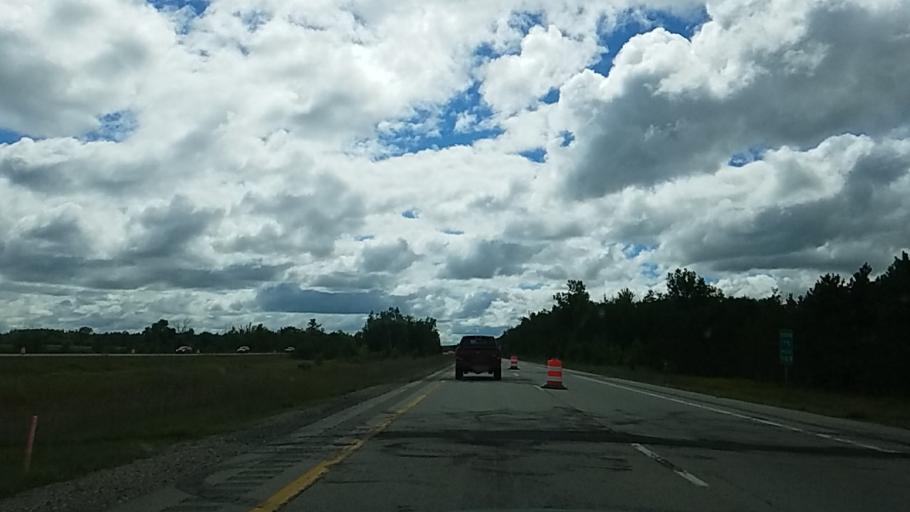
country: US
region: Michigan
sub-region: Arenac County
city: Standish
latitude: 43.9632
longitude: -84.0166
